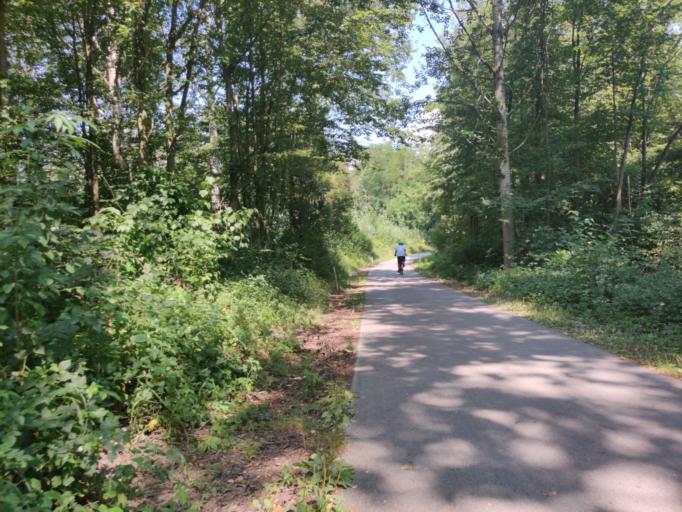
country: AT
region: Upper Austria
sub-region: Politischer Bezirk Urfahr-Umgebung
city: Goldworth
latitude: 48.3172
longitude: 14.1377
